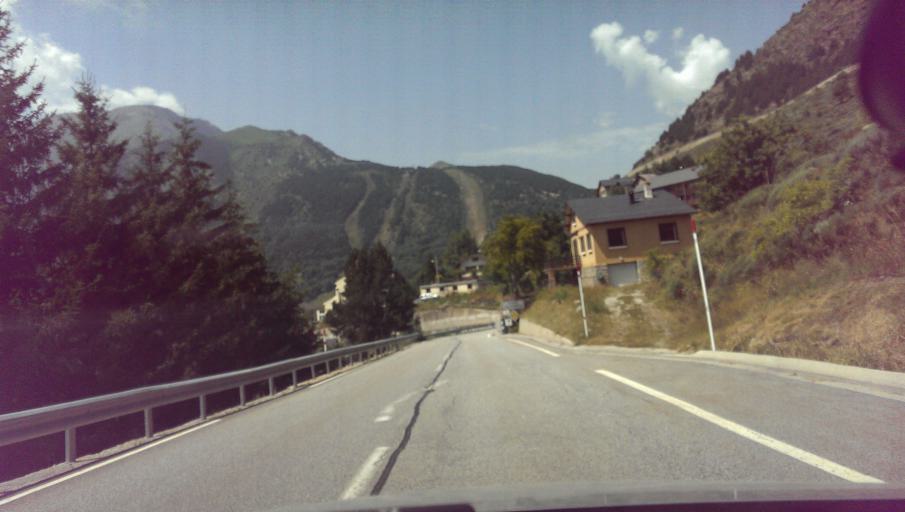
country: AD
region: Encamp
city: Pas de la Casa
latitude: 42.5497
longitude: 1.8338
